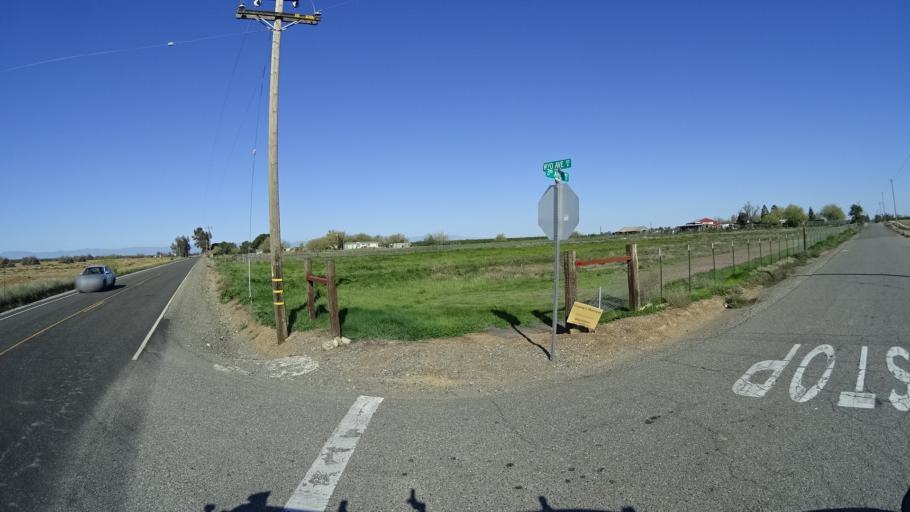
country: US
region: California
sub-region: Glenn County
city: Hamilton City
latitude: 39.7665
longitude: -122.0666
